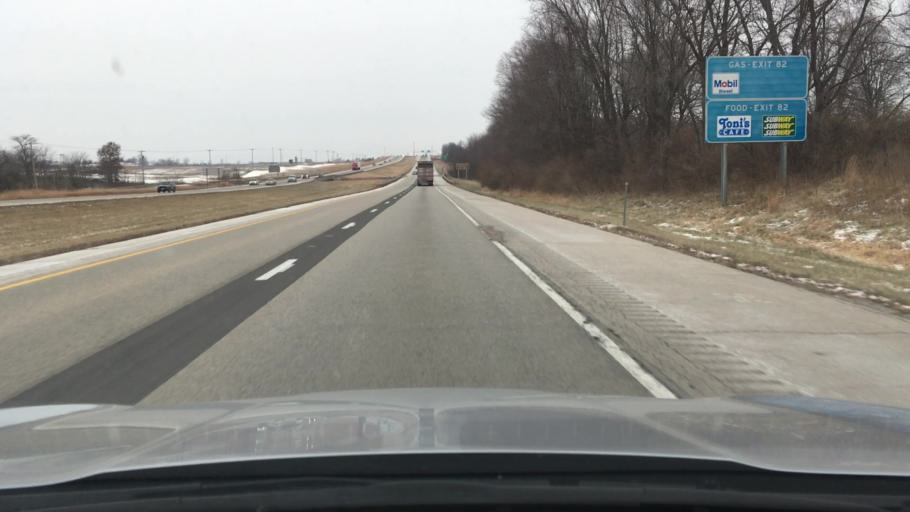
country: US
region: Illinois
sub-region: Sangamon County
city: Divernon
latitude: 39.5777
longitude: -89.6462
